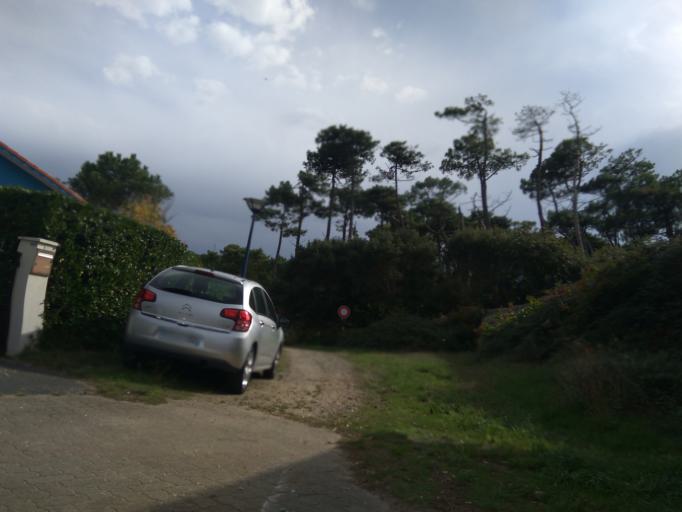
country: FR
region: Aquitaine
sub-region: Departement des Landes
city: Capbreton
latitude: 43.6336
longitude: -1.4445
